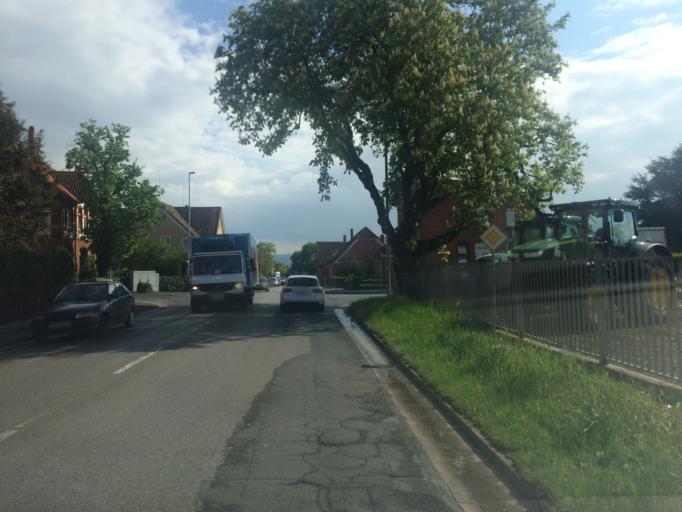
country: DE
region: Lower Saxony
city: Gross Munzel
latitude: 52.3678
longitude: 9.4791
